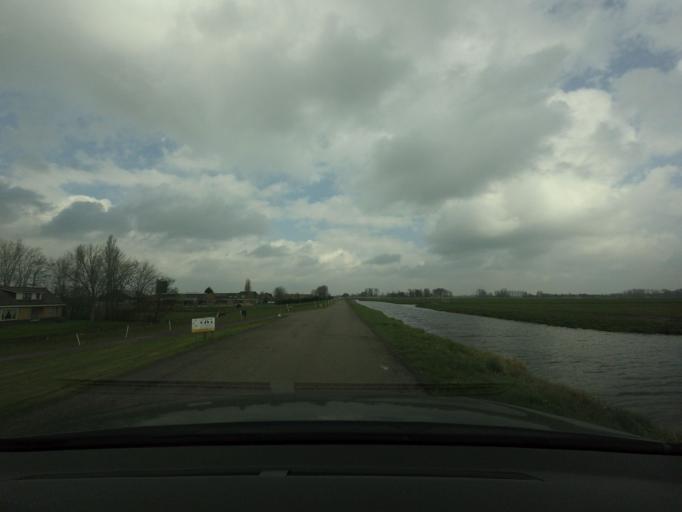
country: NL
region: North Holland
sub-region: Gemeente Uithoorn
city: Uithoorn
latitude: 52.1997
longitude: 4.8034
